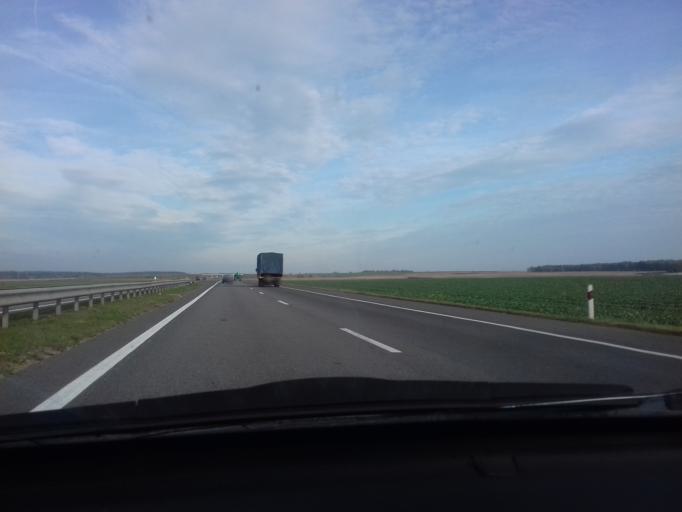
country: BY
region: Minsk
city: Machulishchy
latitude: 53.7381
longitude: 27.5943
